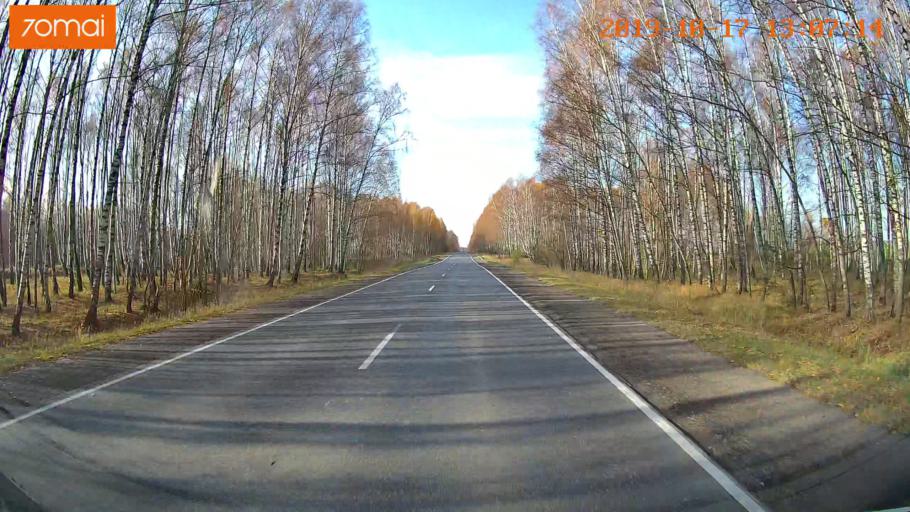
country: RU
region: Rjazan
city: Syntul
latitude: 54.9807
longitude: 41.2953
